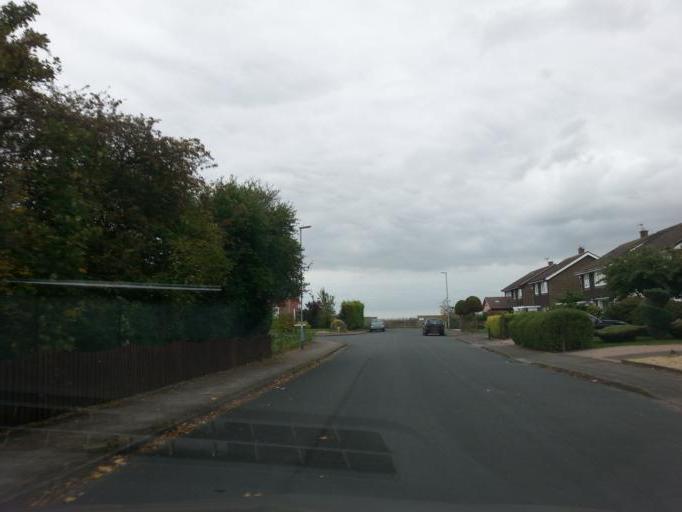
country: GB
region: England
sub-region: Nottinghamshire
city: Newark on Trent
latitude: 53.0739
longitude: -0.7793
